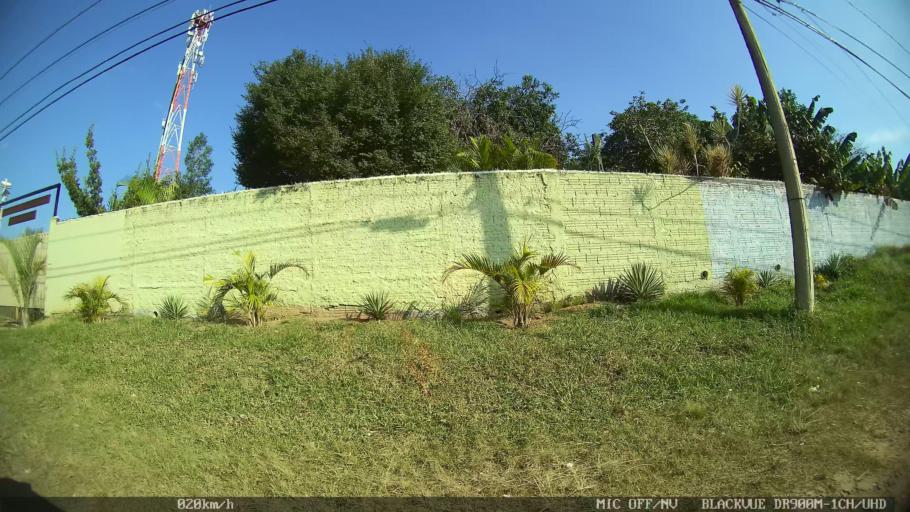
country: BR
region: Sao Paulo
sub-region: Campinas
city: Campinas
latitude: -22.9851
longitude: -47.1463
